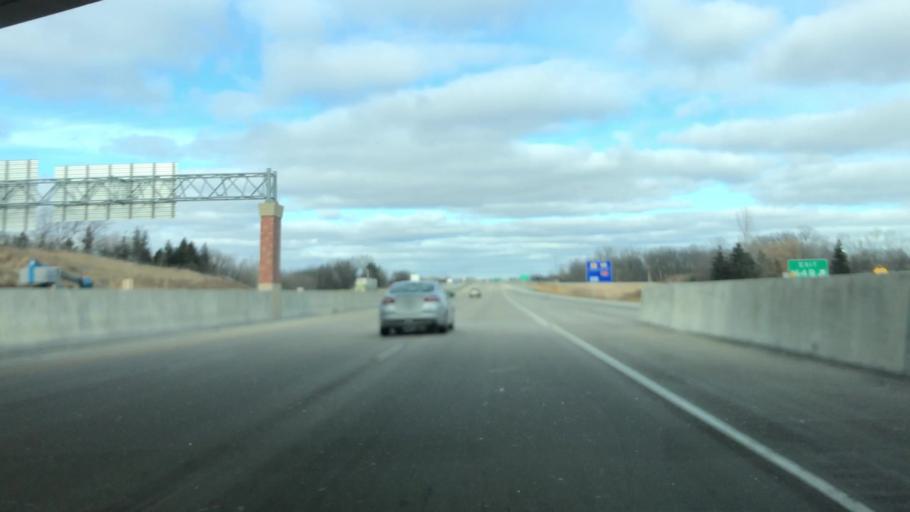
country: US
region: Wisconsin
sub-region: Brown County
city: Ashwaubenon
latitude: 44.4780
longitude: -88.0799
